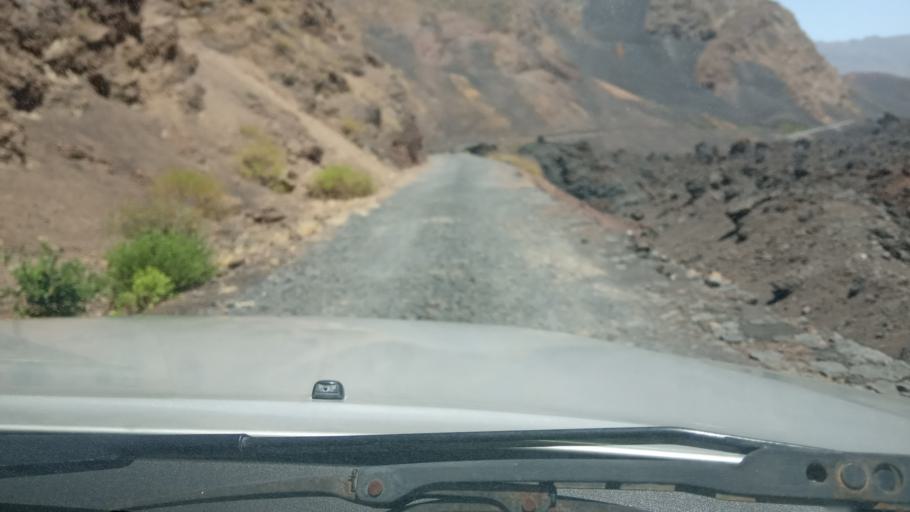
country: CV
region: Santa Catarina do Fogo
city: Cova Figueira
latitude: 14.9161
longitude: -24.3409
